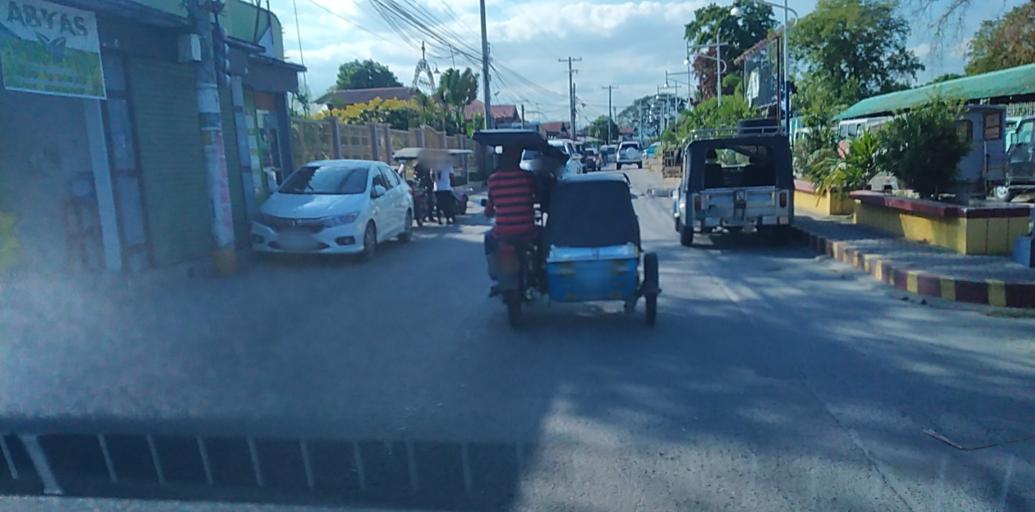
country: PH
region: Central Luzon
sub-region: Province of Pampanga
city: Acli
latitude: 15.1154
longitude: 120.6364
